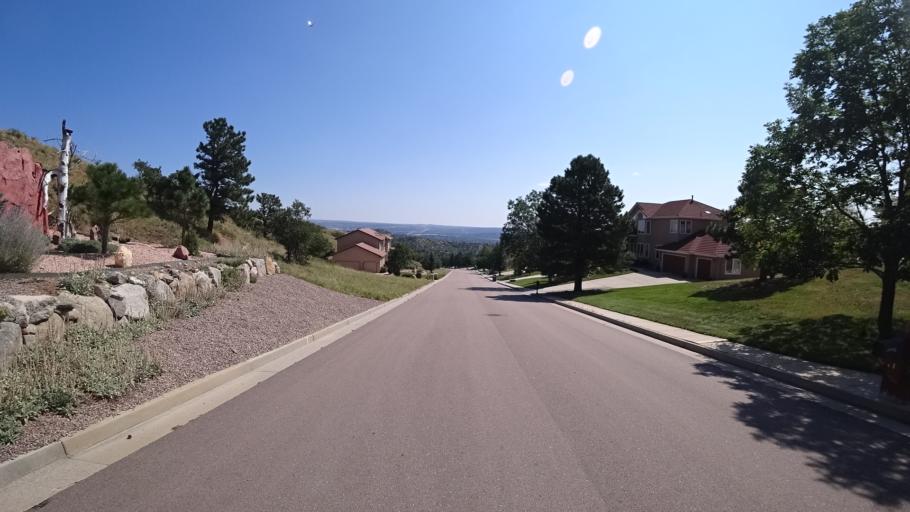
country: US
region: Colorado
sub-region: El Paso County
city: Air Force Academy
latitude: 38.9230
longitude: -104.8749
